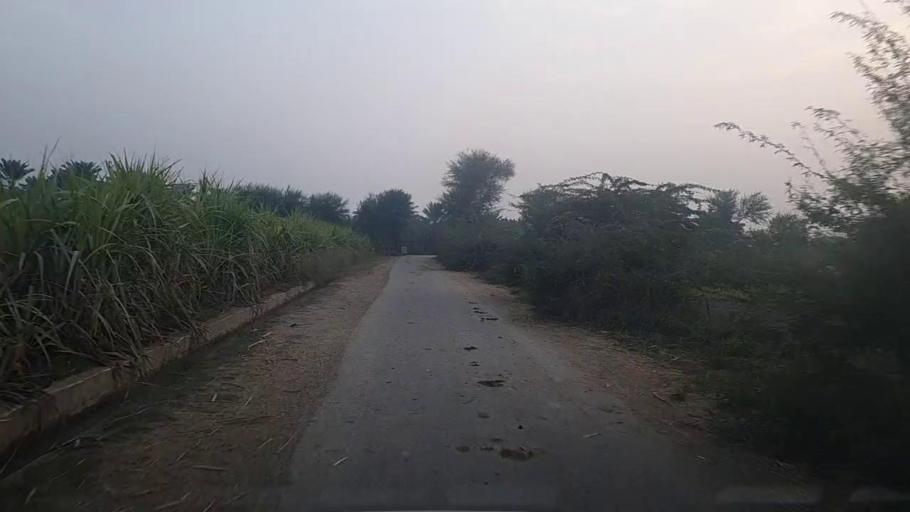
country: PK
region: Sindh
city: Kot Diji
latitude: 27.3416
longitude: 68.6425
